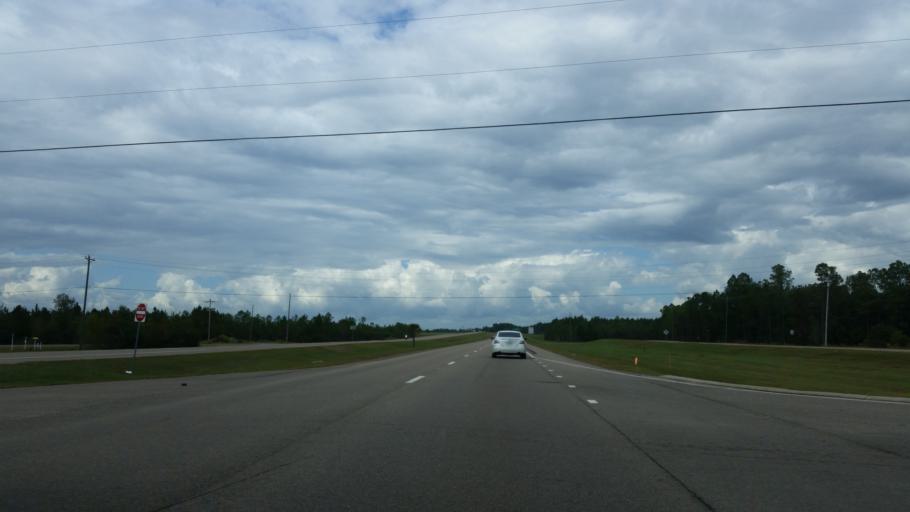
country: US
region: Mississippi
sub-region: Harrison County
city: D'Iberville
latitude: 30.4772
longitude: -88.9104
